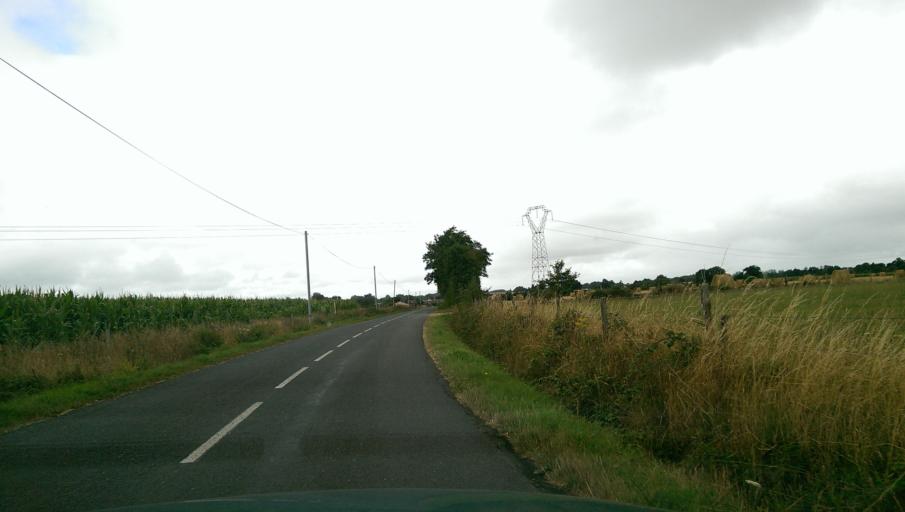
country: FR
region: Pays de la Loire
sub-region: Departement de la Loire-Atlantique
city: La Planche
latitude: 47.0045
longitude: -1.4124
